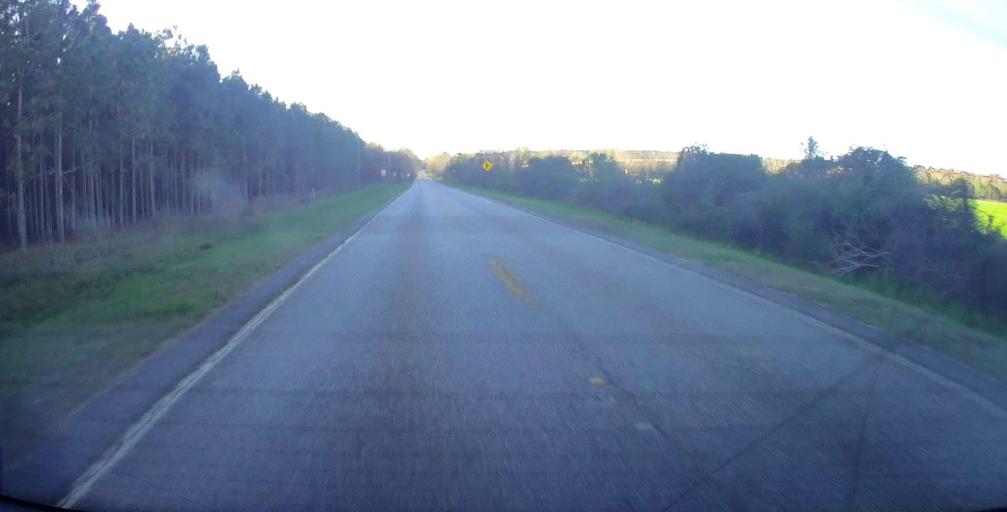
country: US
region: Georgia
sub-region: Wilcox County
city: Abbeville
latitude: 32.1154
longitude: -83.3223
